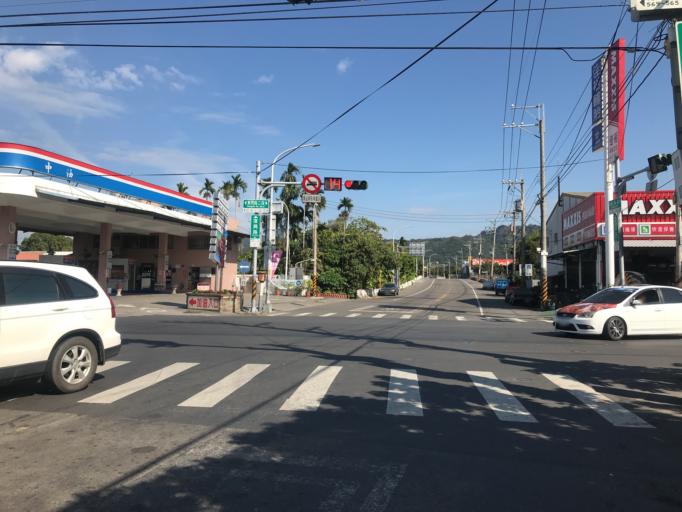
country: TW
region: Taiwan
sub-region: Nantou
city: Nantou
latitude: 23.8622
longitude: 120.5931
